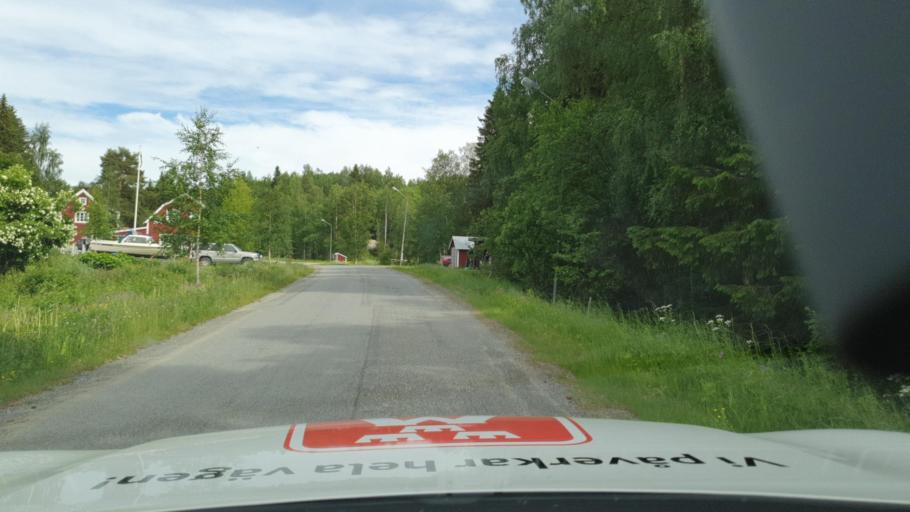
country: SE
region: Vaesterbotten
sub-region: Skelleftea Kommun
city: Burtraesk
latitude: 64.4822
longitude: 20.5262
